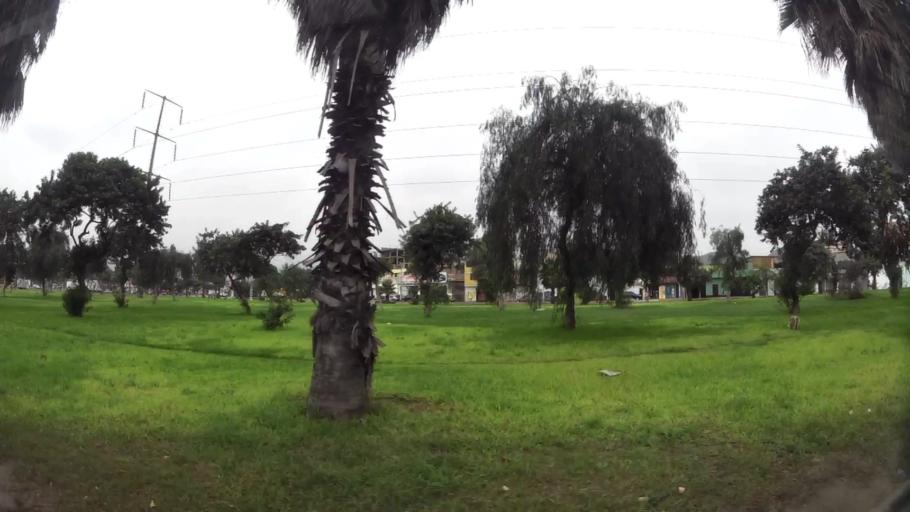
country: PE
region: Lima
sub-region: Lima
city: Independencia
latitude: -11.9925
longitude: -77.0833
